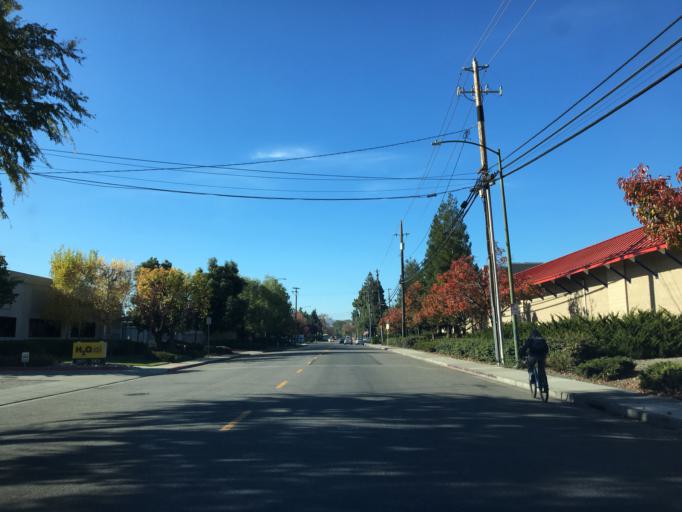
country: US
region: California
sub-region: Santa Clara County
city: Mountain View
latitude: 37.4191
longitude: -122.0950
